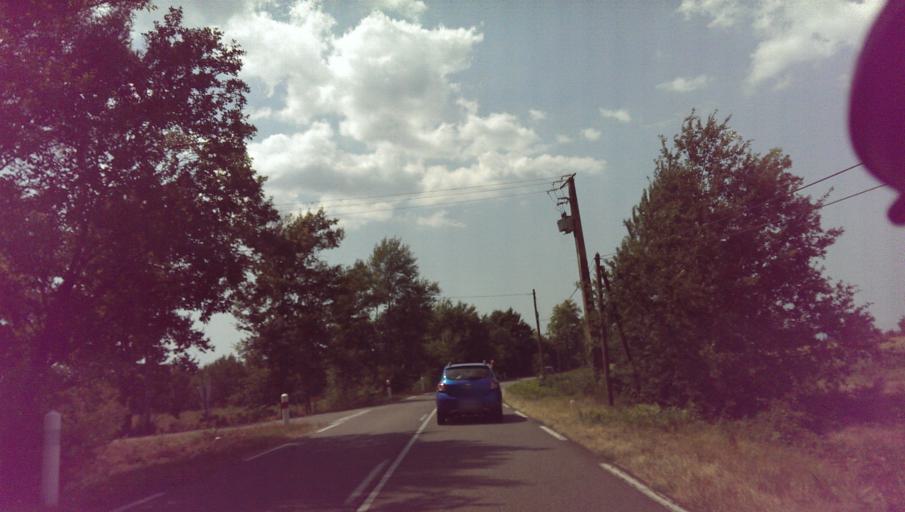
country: FR
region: Aquitaine
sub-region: Departement des Landes
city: Sabres
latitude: 44.1253
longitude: -0.6847
